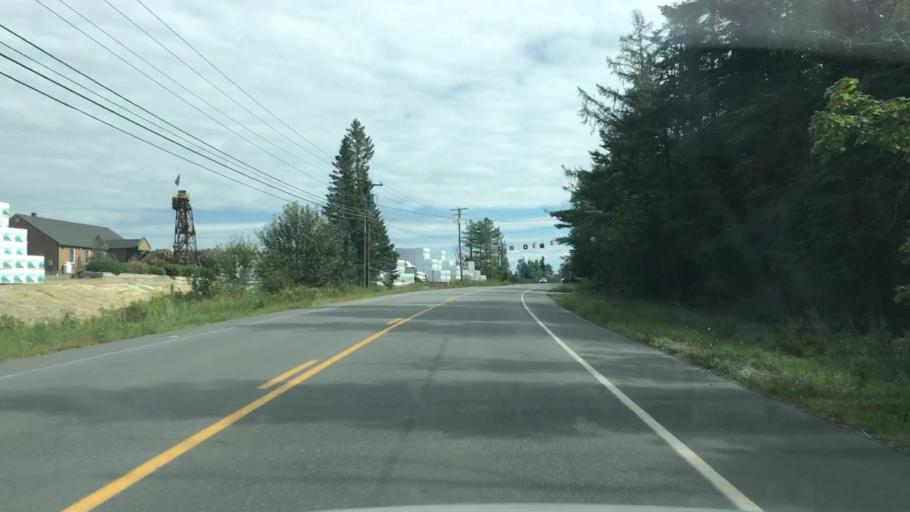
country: US
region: Maine
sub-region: Piscataquis County
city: Dover-Foxcroft
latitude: 45.2007
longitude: -69.1976
